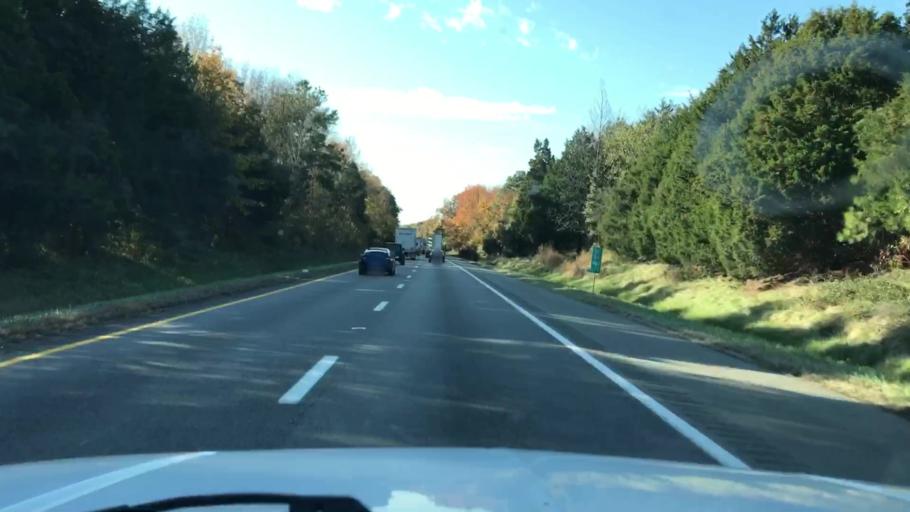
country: US
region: Virginia
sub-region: Henrico County
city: Wyndham
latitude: 37.6958
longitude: -77.7169
